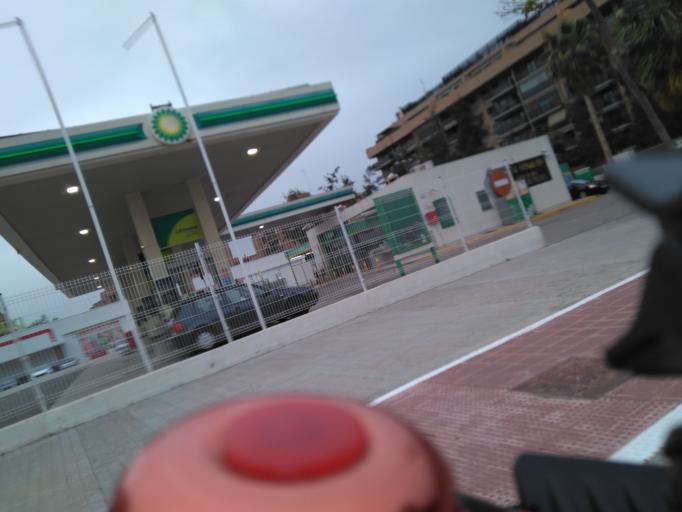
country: ES
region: Valencia
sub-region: Provincia de Valencia
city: Mislata
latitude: 39.4881
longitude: -0.4047
